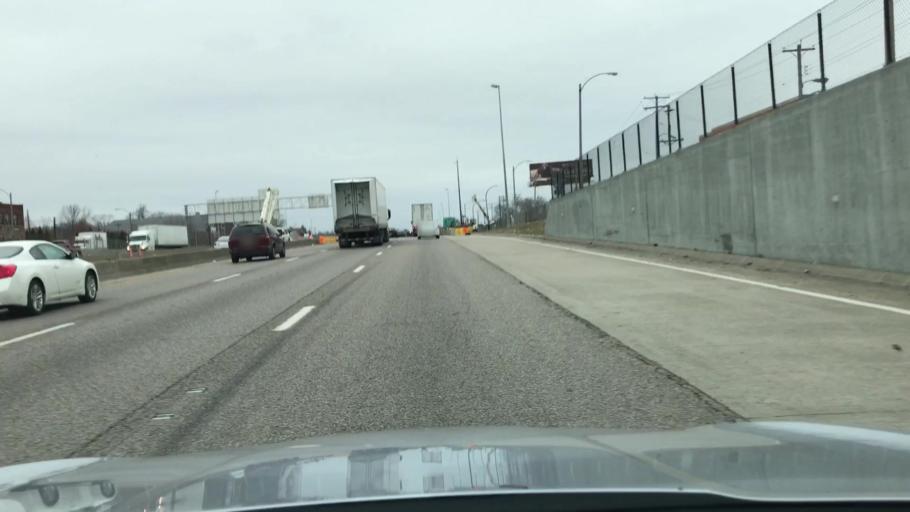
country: US
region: Missouri
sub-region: City of Saint Louis
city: St. Louis
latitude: 38.6478
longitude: -90.1912
